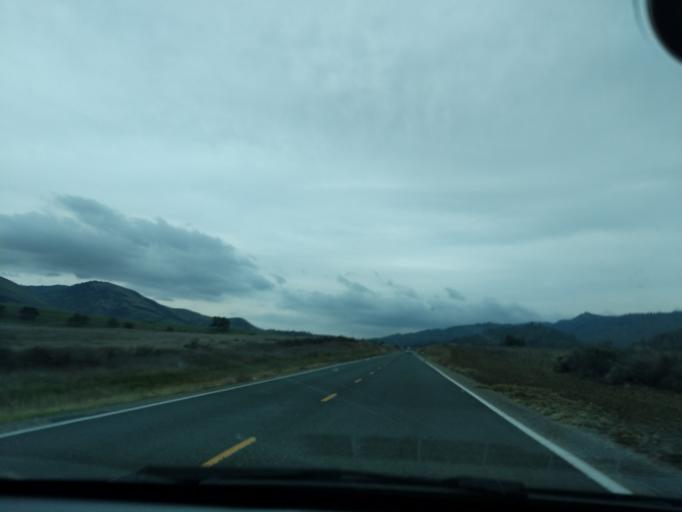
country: US
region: California
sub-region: San Benito County
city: Ridgemark
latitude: 36.6446
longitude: -121.2350
